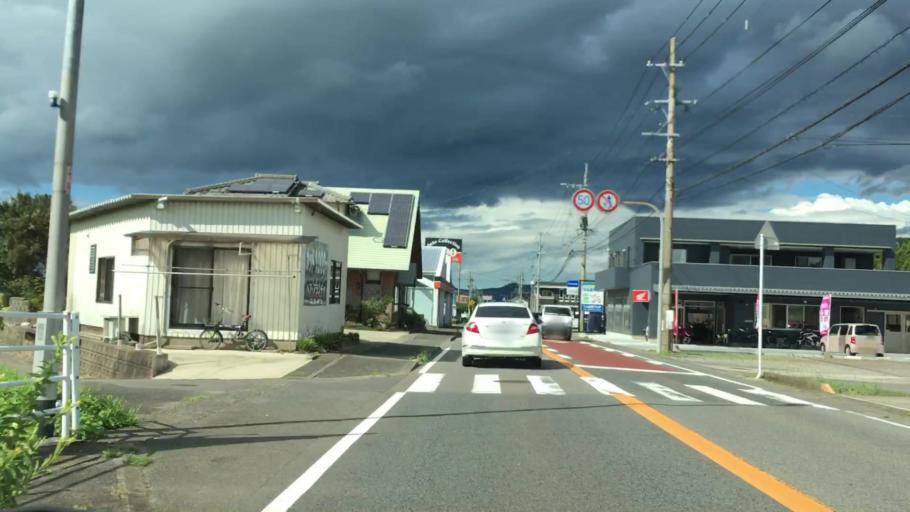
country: JP
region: Saga Prefecture
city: Imaricho-ko
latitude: 33.2484
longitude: 129.8523
